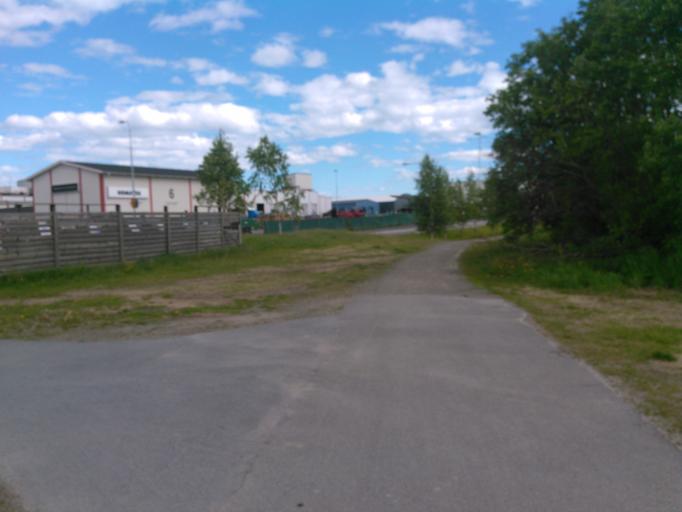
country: SE
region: Vaesterbotten
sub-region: Umea Kommun
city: Umea
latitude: 63.7964
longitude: 20.3016
